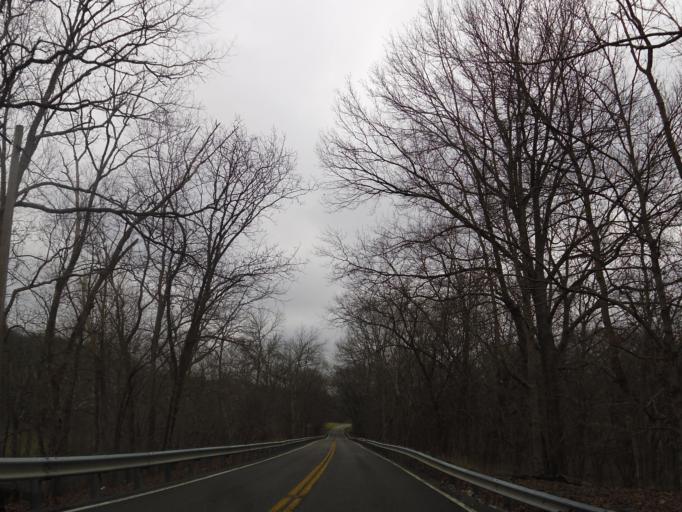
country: US
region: Kentucky
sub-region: Henry County
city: Eminence
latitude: 38.3442
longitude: -85.0000
